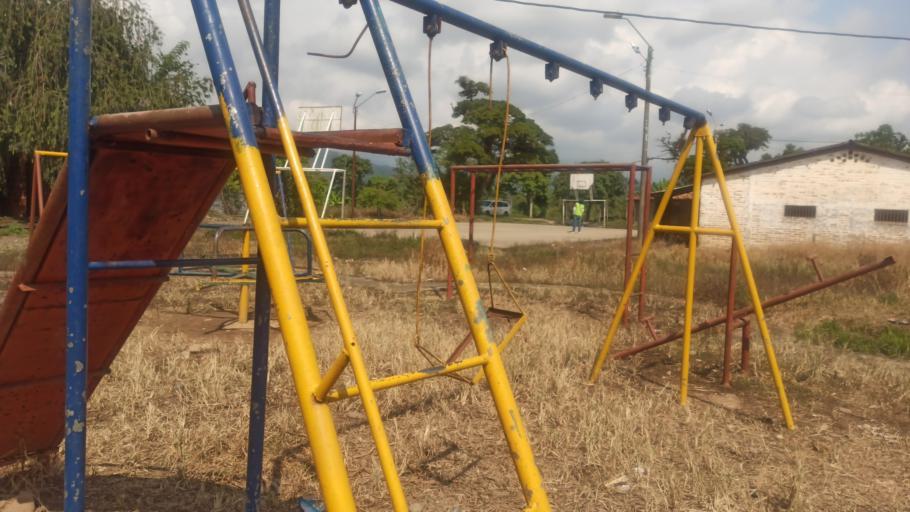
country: CO
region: Cauca
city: Buenos Aires
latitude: 3.1077
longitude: -76.6174
